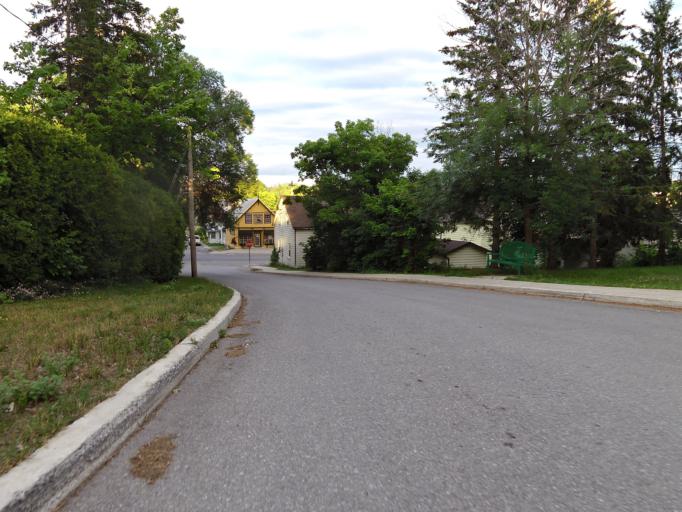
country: CA
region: Ontario
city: Arnprior
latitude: 45.3342
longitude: -76.2910
